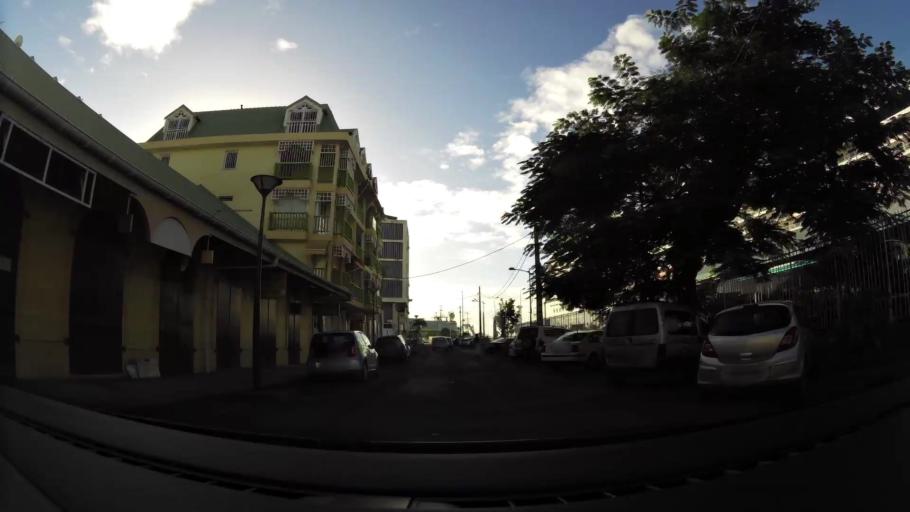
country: GP
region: Guadeloupe
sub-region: Guadeloupe
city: Pointe-a-Pitre
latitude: 16.2369
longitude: -61.5386
